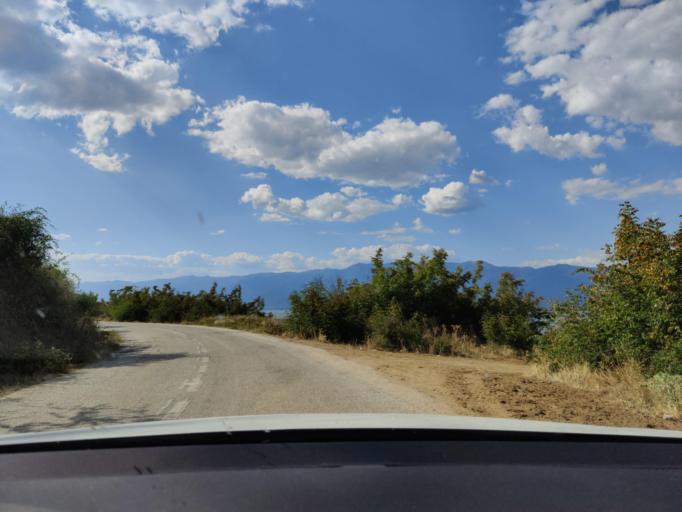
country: GR
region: Central Macedonia
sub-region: Nomos Serron
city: Chrysochorafa
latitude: 41.1509
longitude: 23.2059
